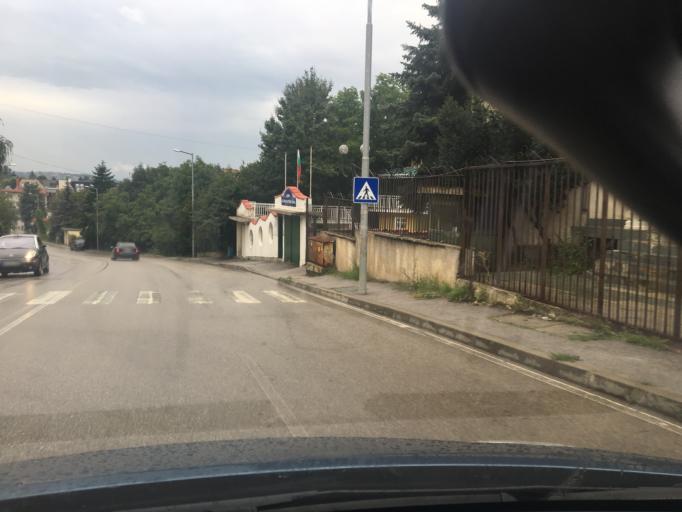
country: BG
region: Sofia-Capital
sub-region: Stolichna Obshtina
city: Sofia
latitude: 42.6463
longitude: 23.2730
